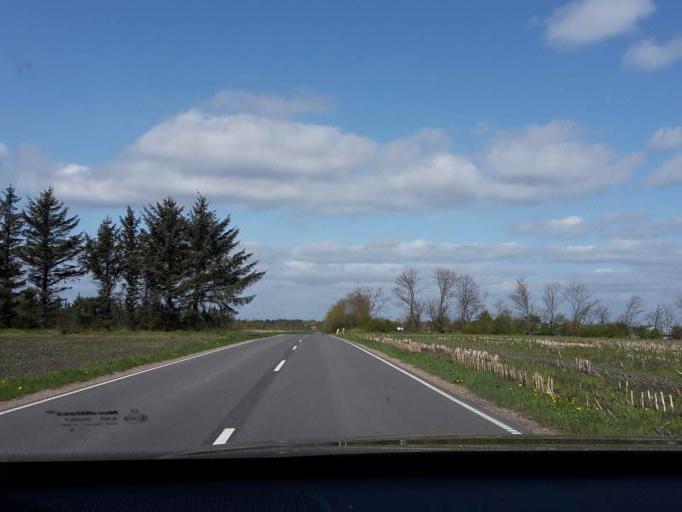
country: DK
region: South Denmark
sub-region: Billund Kommune
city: Grindsted
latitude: 55.6814
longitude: 8.8991
